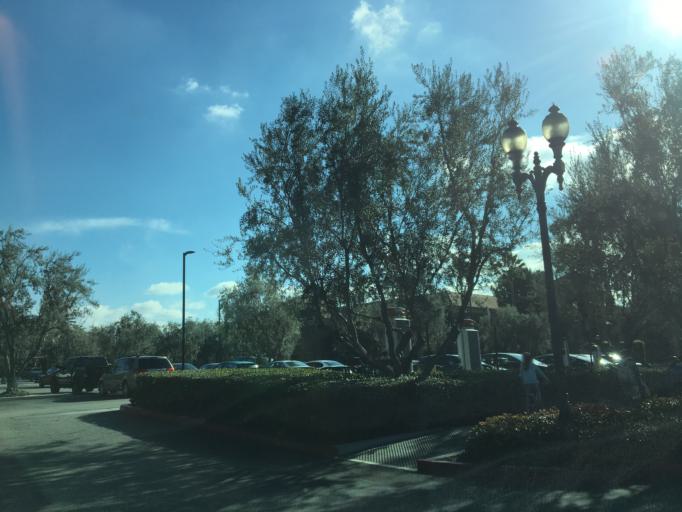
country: US
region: California
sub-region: Orange County
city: Lake Forest
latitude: 33.6990
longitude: -117.7405
